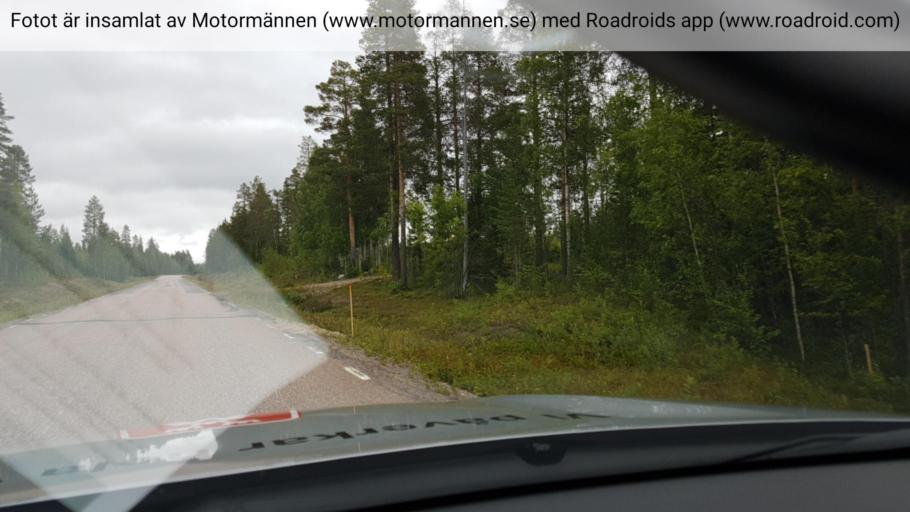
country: SE
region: Norrbotten
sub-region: Overkalix Kommun
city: OEverkalix
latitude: 67.0247
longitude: 22.0019
